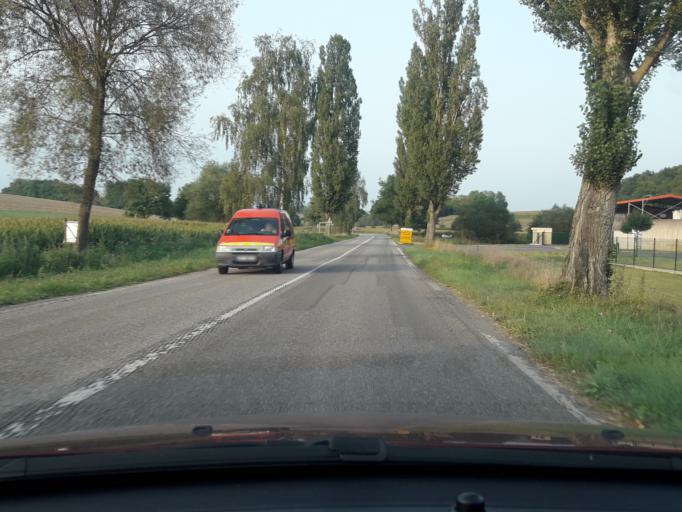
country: FR
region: Alsace
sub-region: Departement du Bas-Rhin
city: Schnersheim
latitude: 48.7041
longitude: 7.5564
